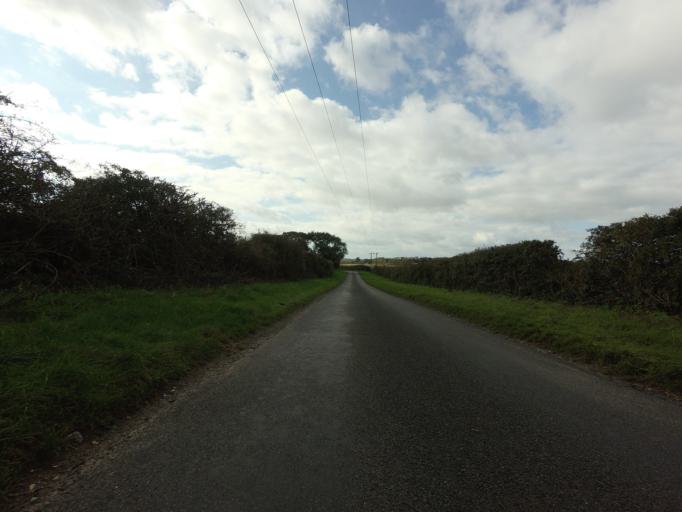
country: GB
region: England
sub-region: Norfolk
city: Hunstanton
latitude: 52.9357
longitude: 0.5813
